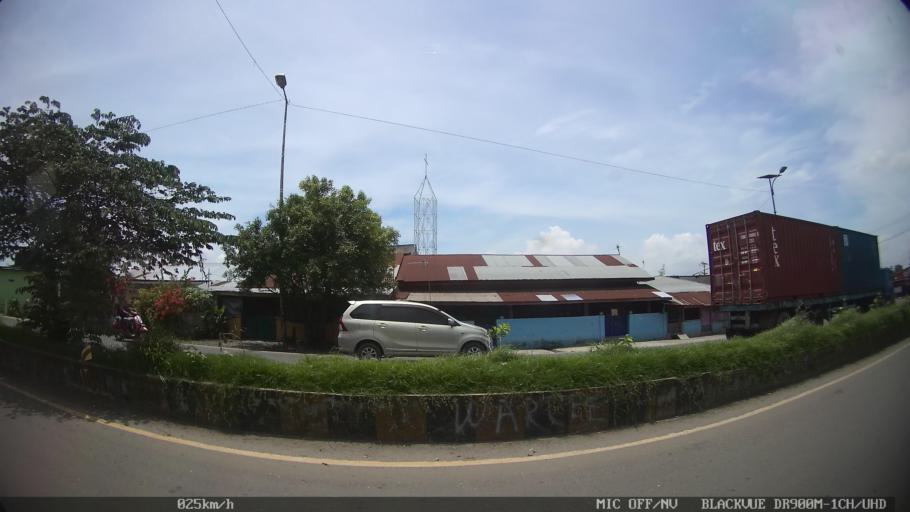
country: ID
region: North Sumatra
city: Belawan
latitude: 3.7715
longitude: 98.6820
